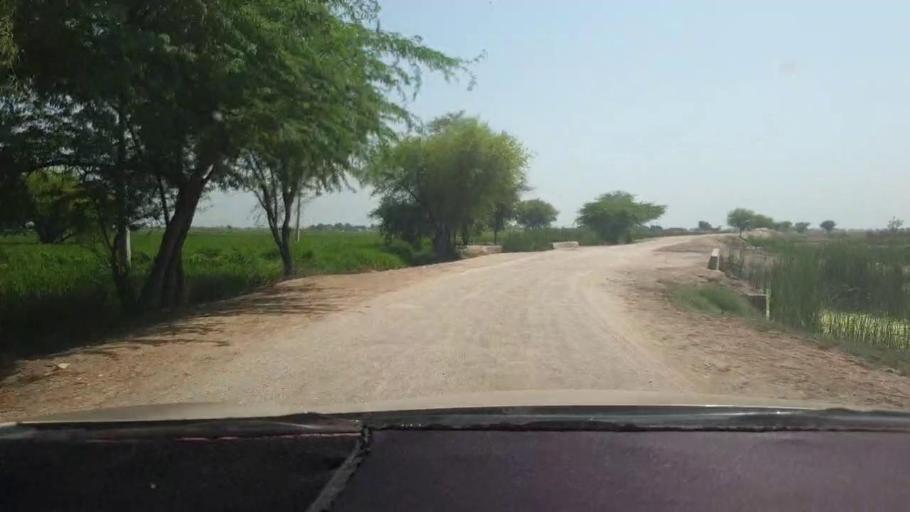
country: PK
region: Sindh
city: Miro Khan
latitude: 27.6805
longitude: 68.0960
